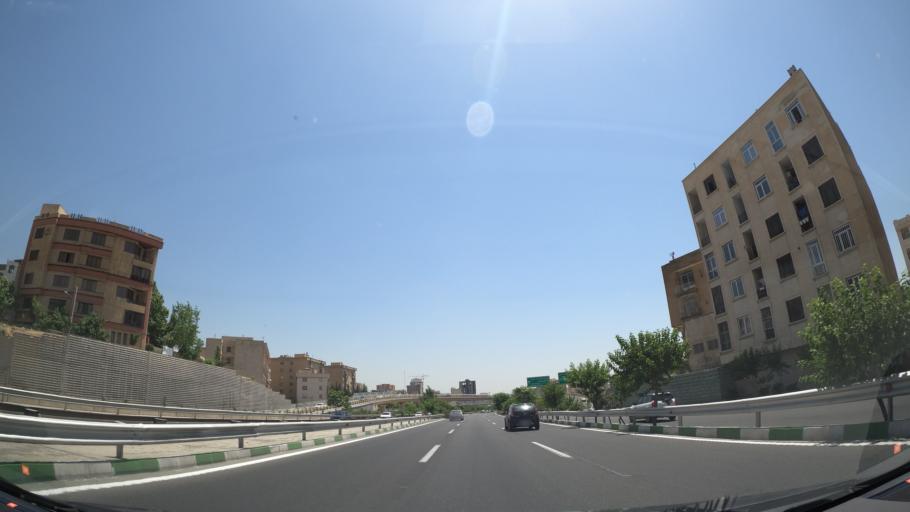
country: IR
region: Tehran
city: Tajrish
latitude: 35.7704
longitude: 51.3210
